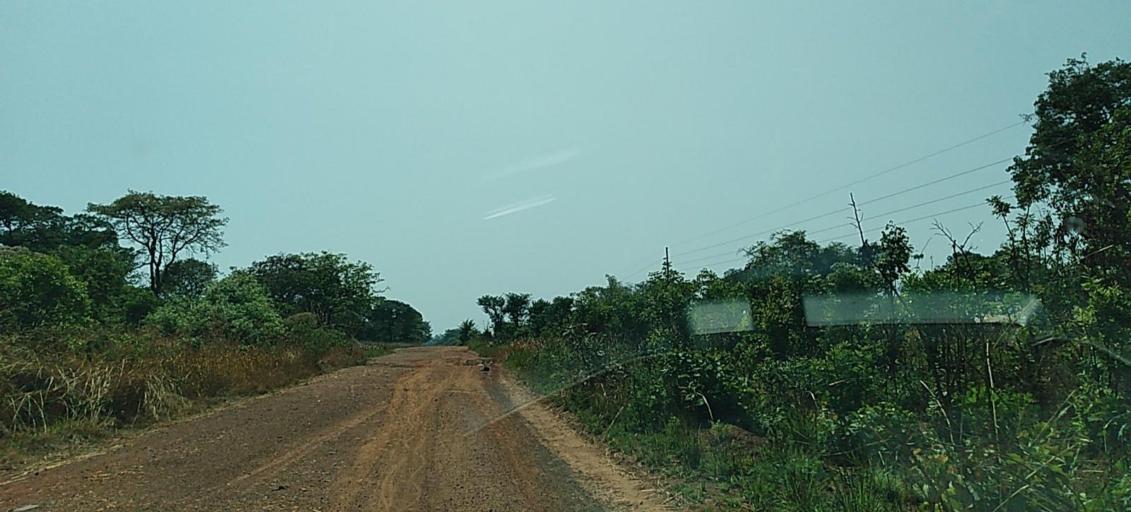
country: ZM
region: North-Western
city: Kansanshi
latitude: -12.0069
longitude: 26.5248
